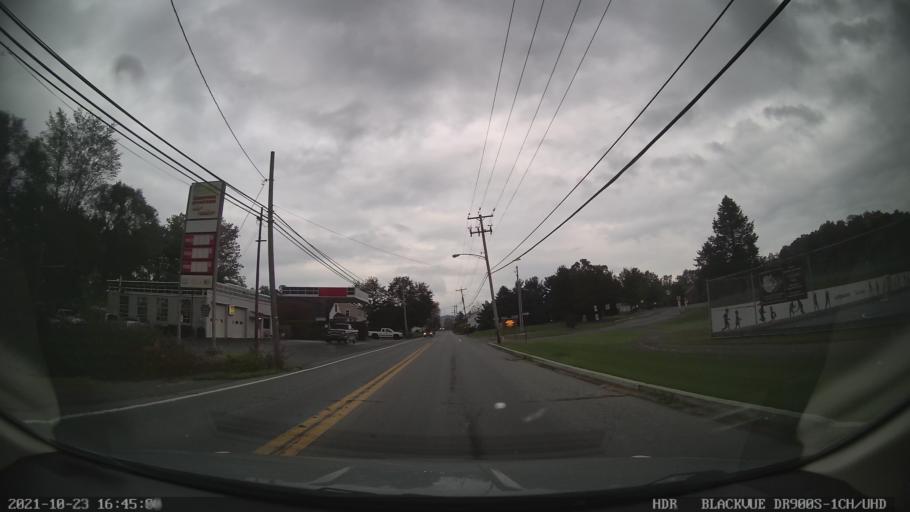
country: US
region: Pennsylvania
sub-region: Berks County
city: Topton
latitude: 40.5045
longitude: -75.6631
